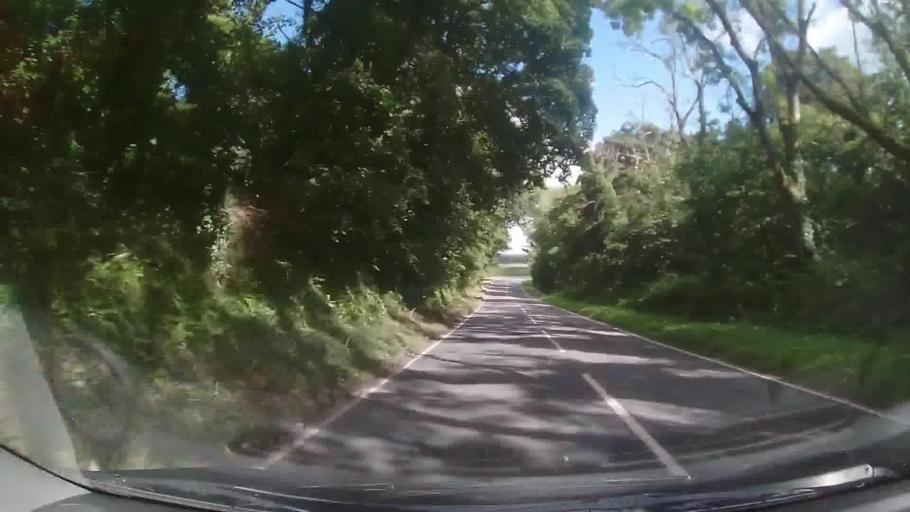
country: GB
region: Wales
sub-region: Pembrokeshire
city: Pembroke
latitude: 51.6843
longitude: -4.8805
